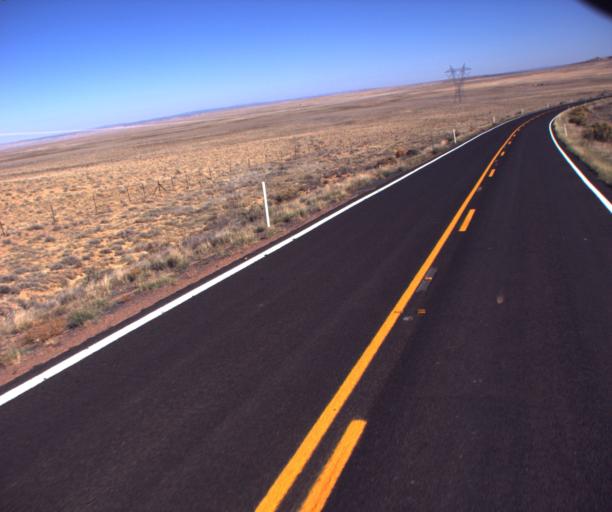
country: US
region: Arizona
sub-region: Coconino County
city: Tuba City
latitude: 35.9689
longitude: -110.8440
